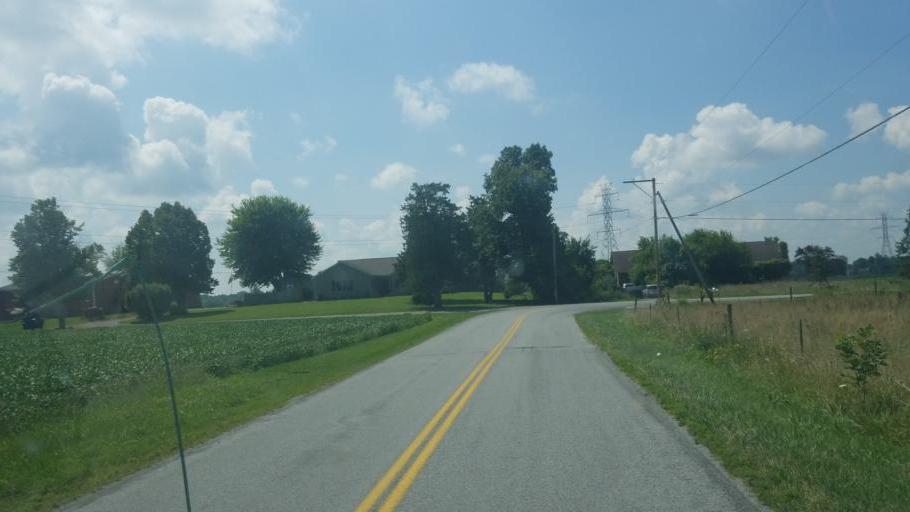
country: US
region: Ohio
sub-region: Allen County
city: Lima
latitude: 40.6995
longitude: -83.9613
